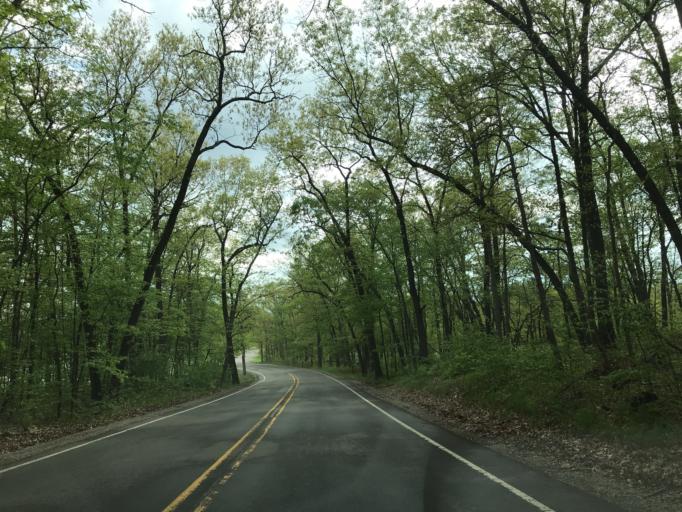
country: US
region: Michigan
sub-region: Oakland County
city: South Lyon
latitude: 42.5293
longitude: -83.6670
